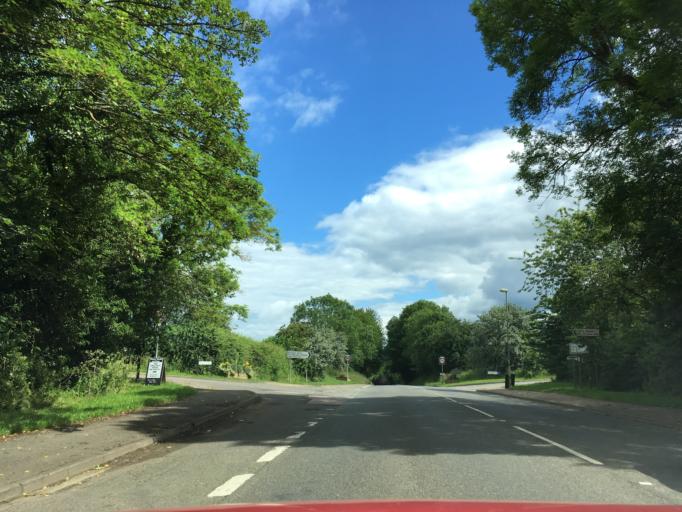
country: GB
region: England
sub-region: Oxfordshire
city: Bloxham
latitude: 52.0277
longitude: -1.3686
